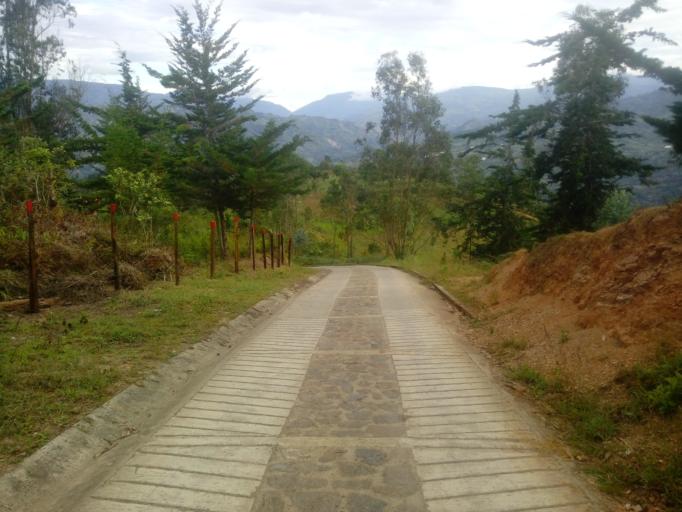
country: CO
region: Cundinamarca
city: Tenza
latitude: 5.1013
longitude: -73.4176
